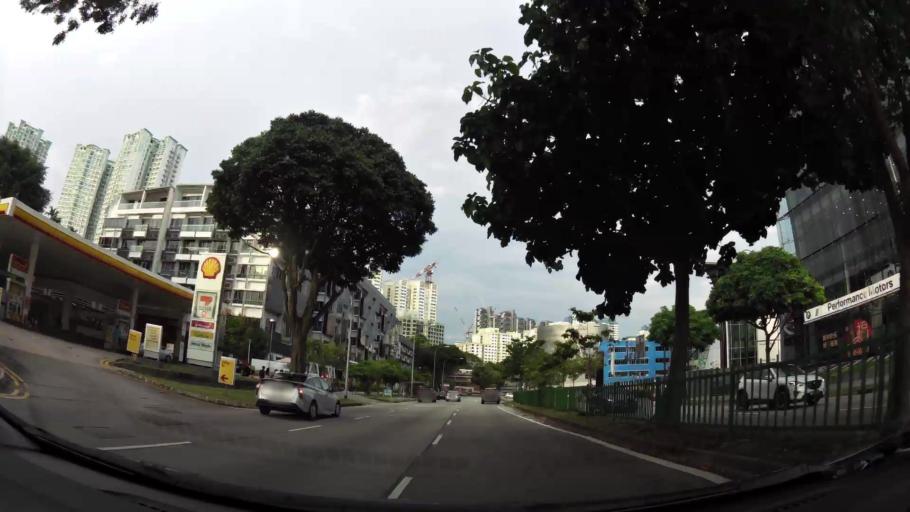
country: SG
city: Singapore
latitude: 1.2904
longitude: 103.8071
